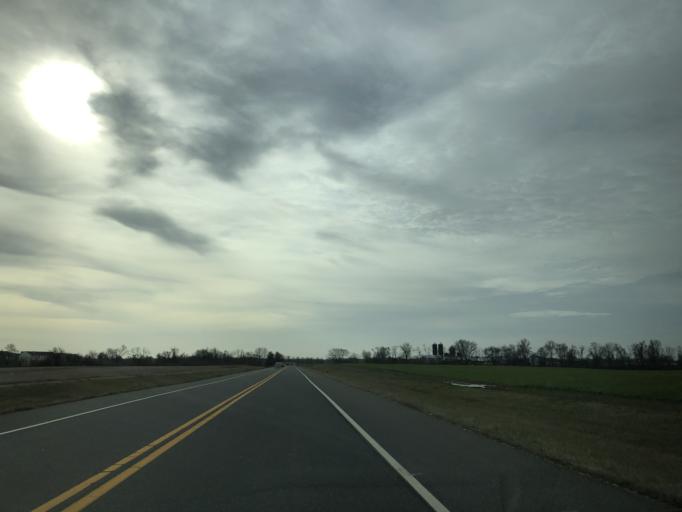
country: US
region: Delaware
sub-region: New Castle County
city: Middletown
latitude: 39.5187
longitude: -75.6791
